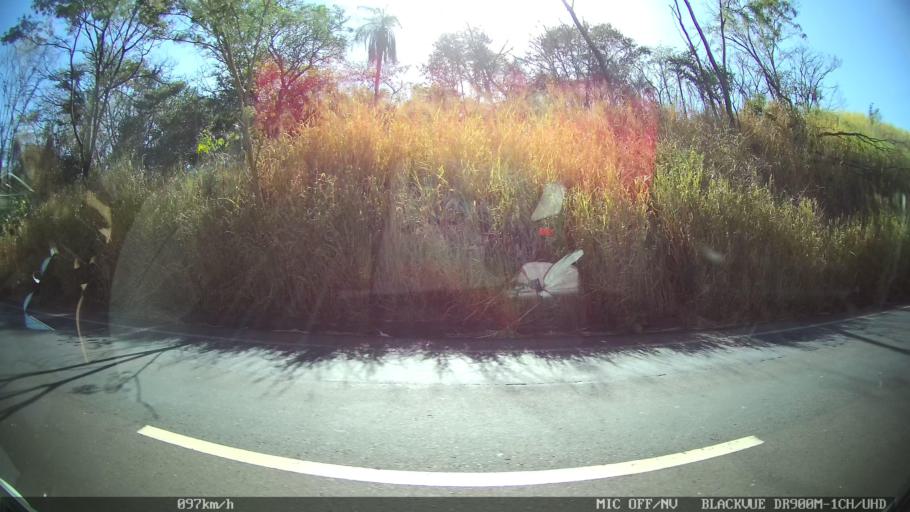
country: BR
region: Sao Paulo
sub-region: Barretos
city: Barretos
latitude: -20.5965
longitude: -48.7189
